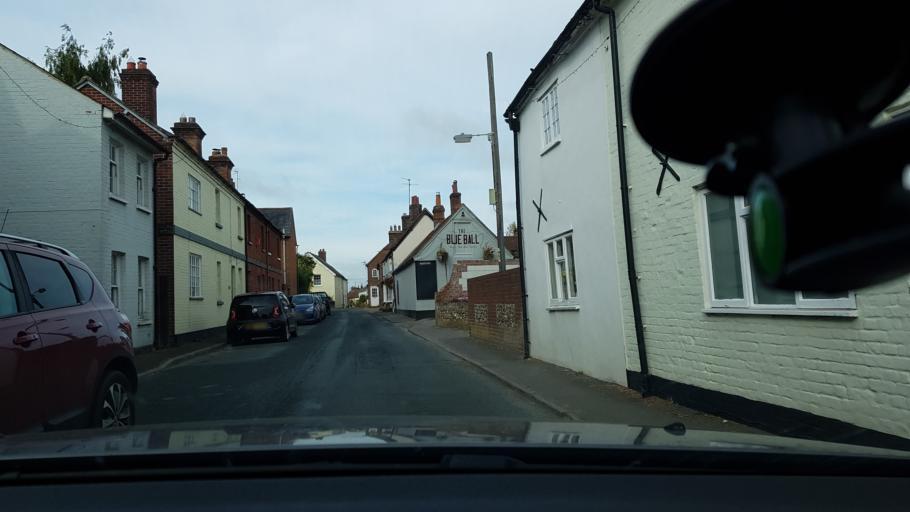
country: GB
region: England
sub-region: West Berkshire
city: Kintbury
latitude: 51.3994
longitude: -1.4525
